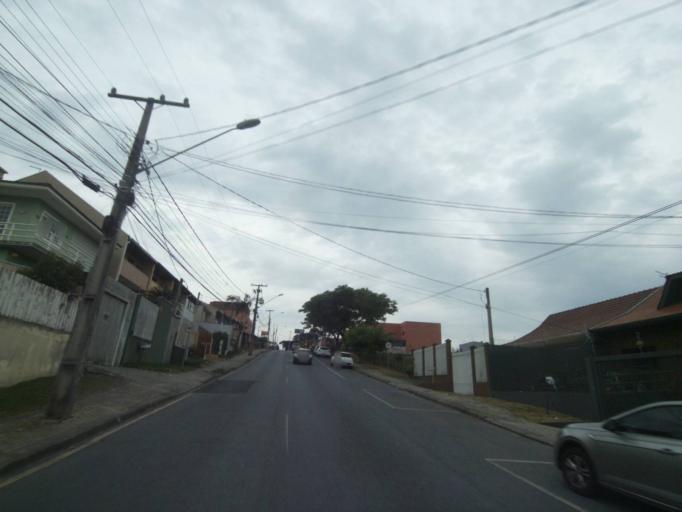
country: BR
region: Parana
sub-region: Sao Jose Dos Pinhais
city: Sao Jose dos Pinhais
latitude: -25.4850
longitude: -49.2219
